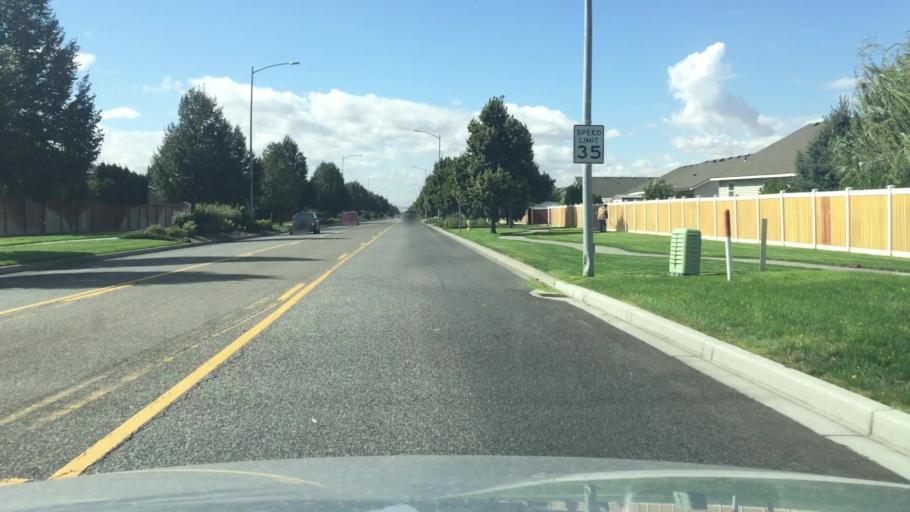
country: US
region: Washington
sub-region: Franklin County
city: West Pasco
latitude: 46.2780
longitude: -119.1917
